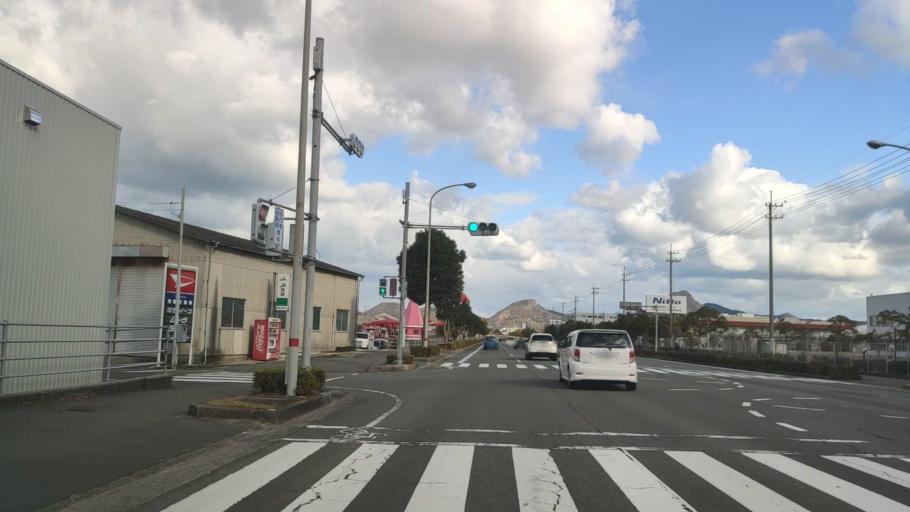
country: JP
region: Ehime
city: Hojo
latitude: 33.9597
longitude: 132.7771
